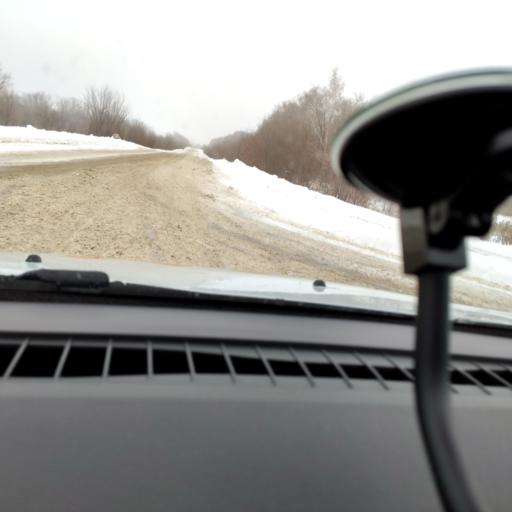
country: RU
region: Samara
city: Dubovyy Umet
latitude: 53.0311
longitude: 50.2189
